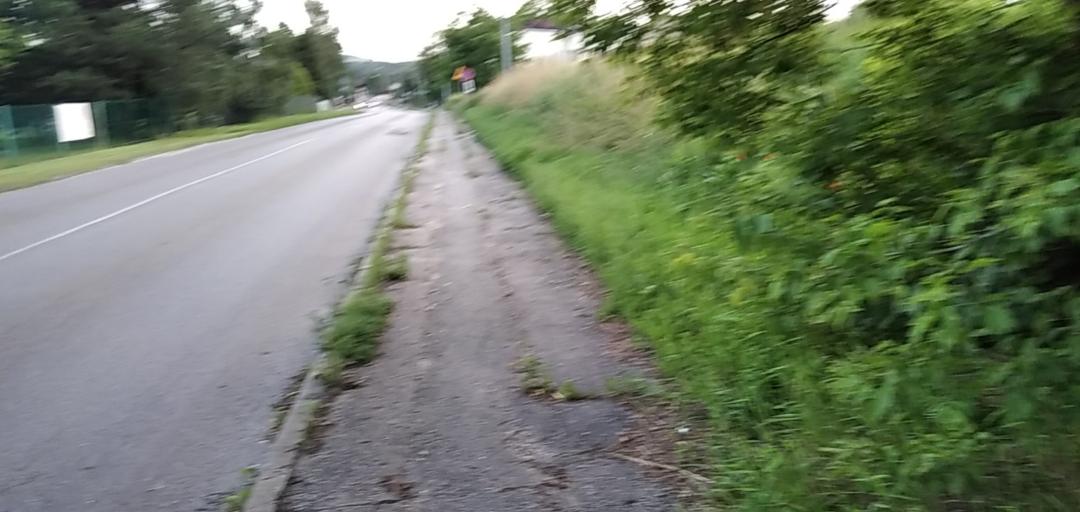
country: PL
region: Silesian Voivodeship
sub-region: Powiat bedzinski
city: Sarnow
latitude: 50.4082
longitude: 19.1399
